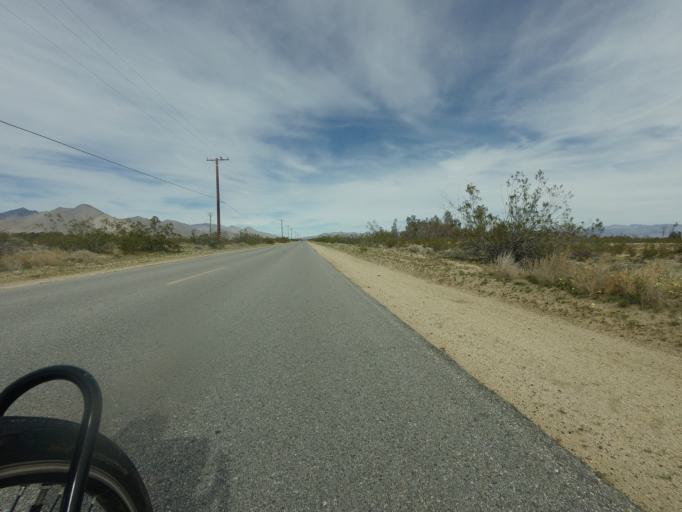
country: US
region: California
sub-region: Kern County
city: Inyokern
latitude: 35.7360
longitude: -117.8387
